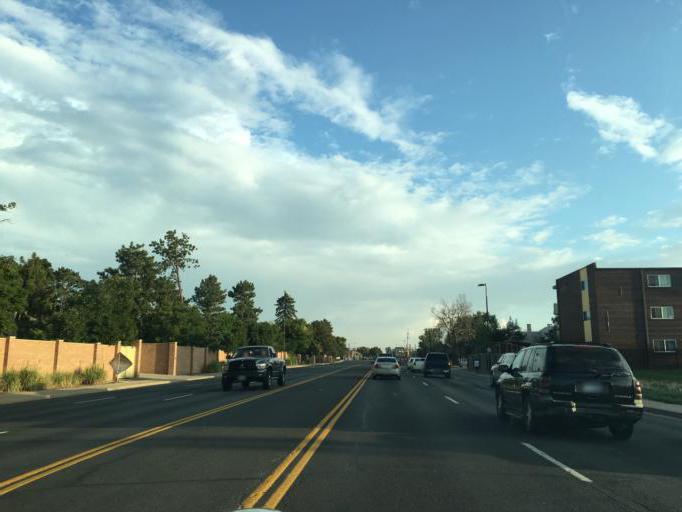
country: US
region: Colorado
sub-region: Adams County
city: Aurora
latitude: 39.7434
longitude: -104.8470
